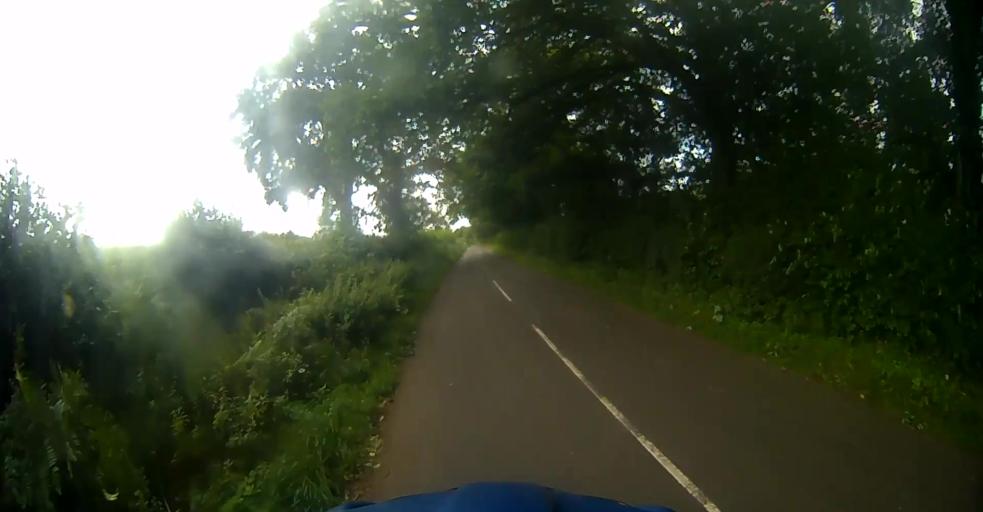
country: GB
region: England
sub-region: Hampshire
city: Alton
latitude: 51.1843
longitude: -1.0199
